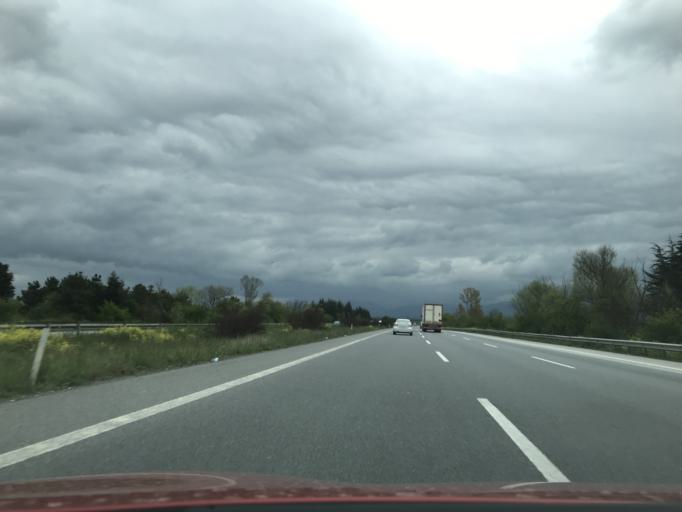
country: TR
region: Duzce
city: Cilimli
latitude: 40.8411
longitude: 31.0245
